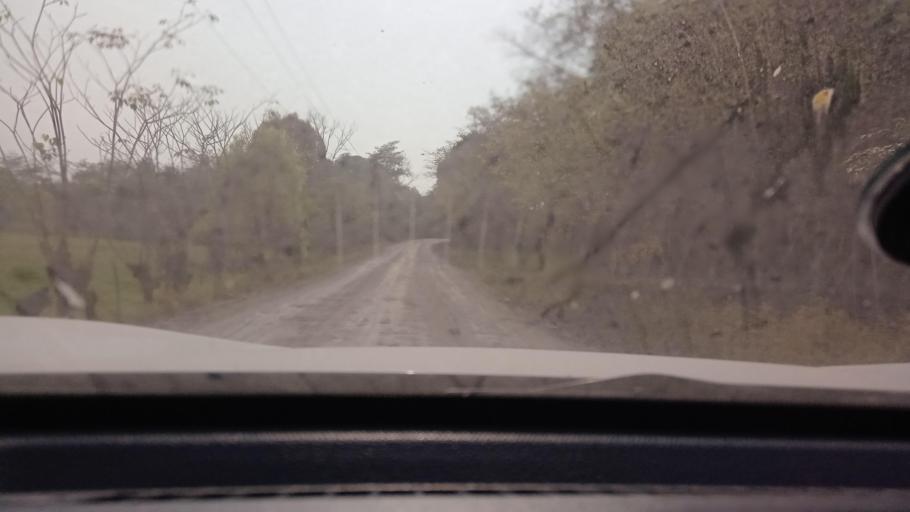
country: MX
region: Tabasco
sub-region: Huimanguillo
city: Francisco Rueda
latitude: 17.6206
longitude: -93.9492
